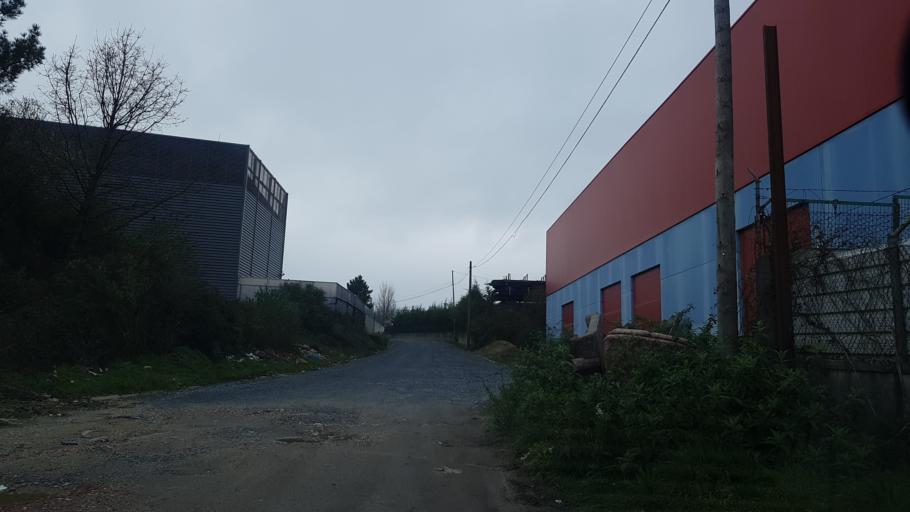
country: ES
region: Galicia
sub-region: Provincia de Lugo
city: Lugo
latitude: 43.0449
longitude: -7.5668
